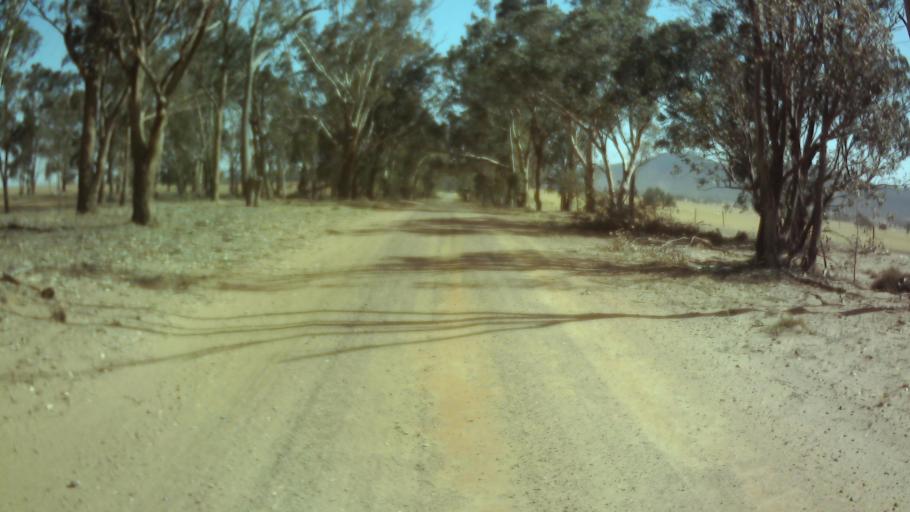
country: AU
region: New South Wales
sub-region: Weddin
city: Grenfell
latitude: -33.8483
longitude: 148.0169
